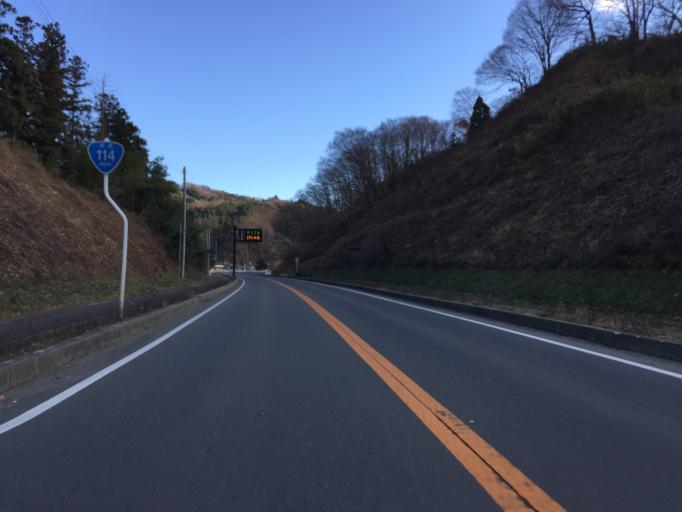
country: JP
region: Fukushima
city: Fukushima-shi
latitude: 37.6596
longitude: 140.6023
